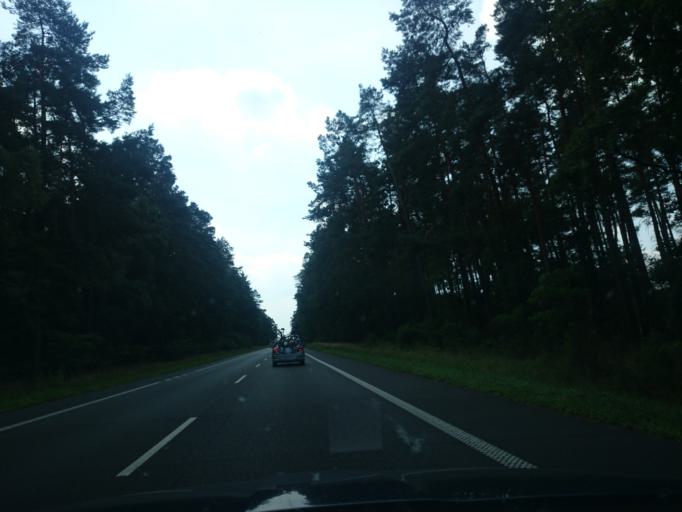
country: PL
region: West Pomeranian Voivodeship
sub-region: Powiat goleniowski
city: Goleniow
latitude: 53.6359
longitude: 14.8177
